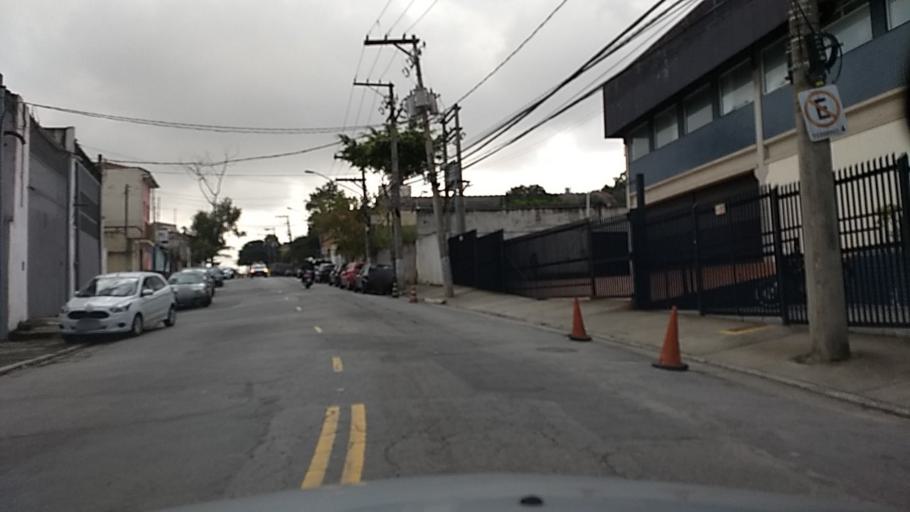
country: BR
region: Sao Paulo
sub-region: Sao Paulo
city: Sao Paulo
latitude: -23.5067
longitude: -46.6117
